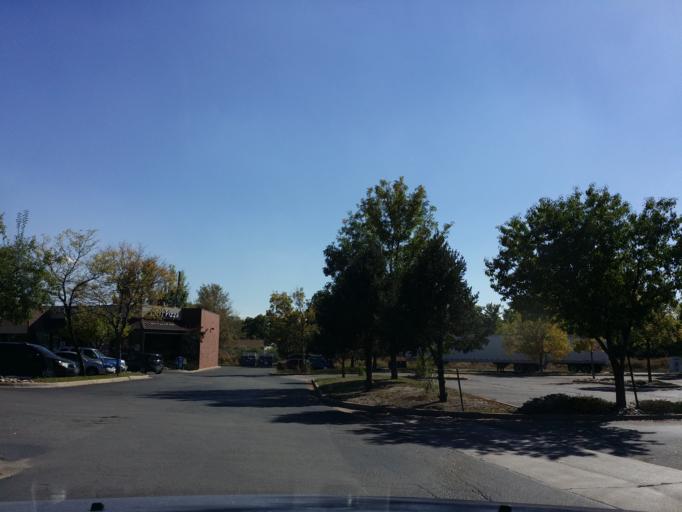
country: US
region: Colorado
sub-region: Adams County
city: Westminster
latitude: 39.8561
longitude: -105.0609
